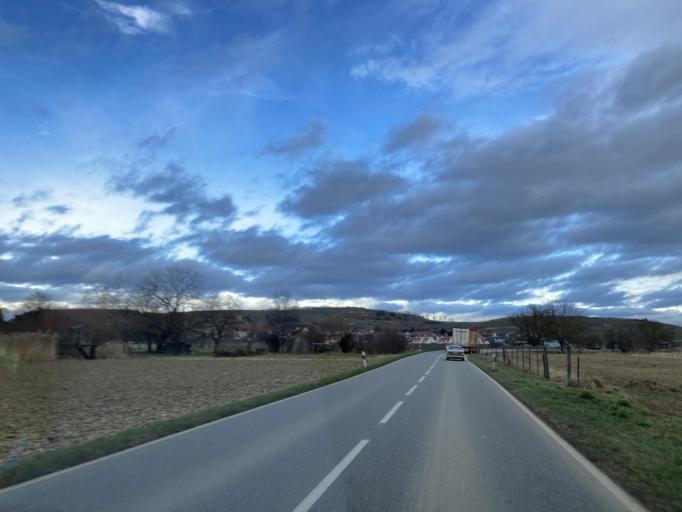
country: DE
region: Baden-Wuerttemberg
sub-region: Freiburg Region
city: Vogtsburg
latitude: 48.0931
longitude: 7.6039
